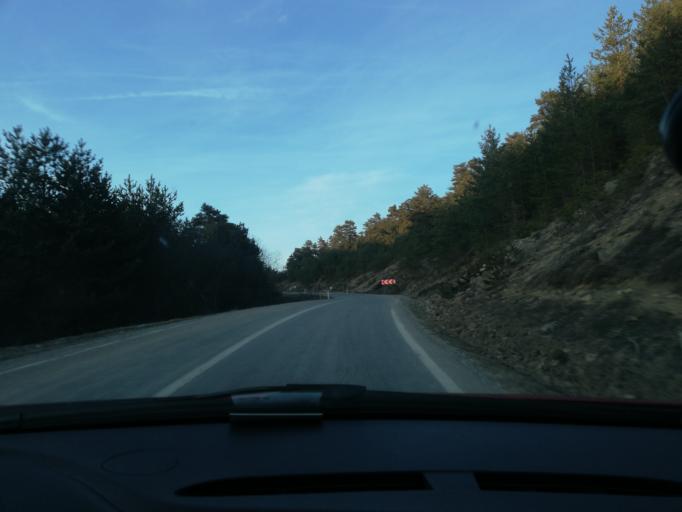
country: TR
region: Kastamonu
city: Agli
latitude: 41.7099
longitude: 33.6530
